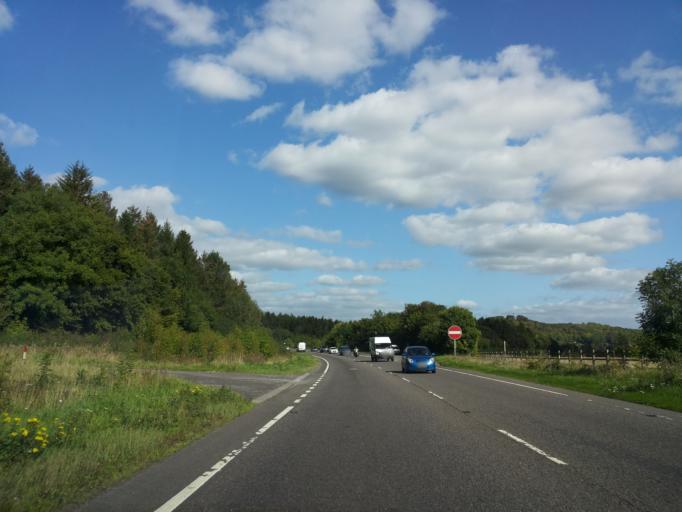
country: GB
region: England
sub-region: Wiltshire
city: Upton Scudamore
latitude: 51.2095
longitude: -2.2067
